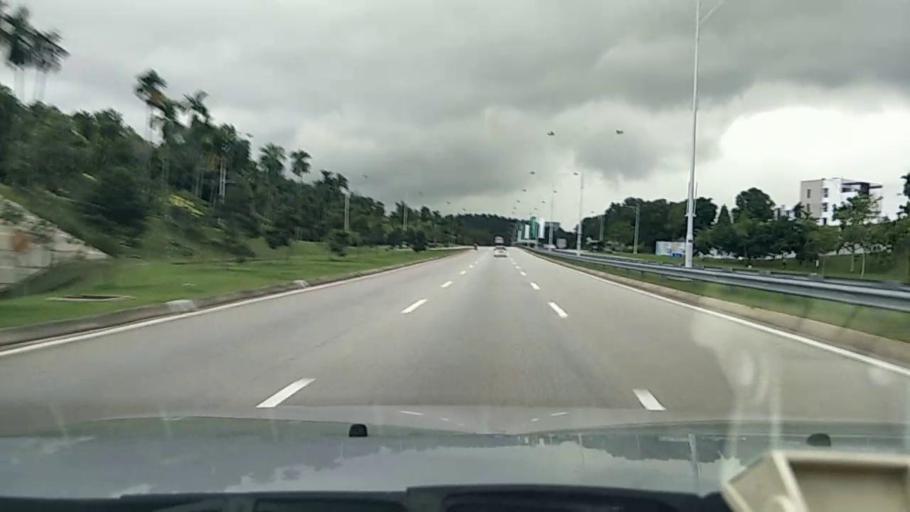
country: MY
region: Putrajaya
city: Putrajaya
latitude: 2.9432
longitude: 101.7140
